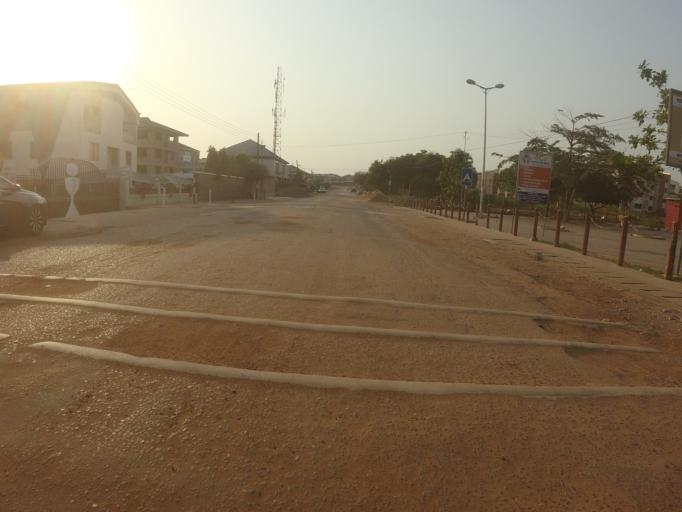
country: GH
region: Greater Accra
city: Nungua
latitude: 5.6235
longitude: -0.0615
